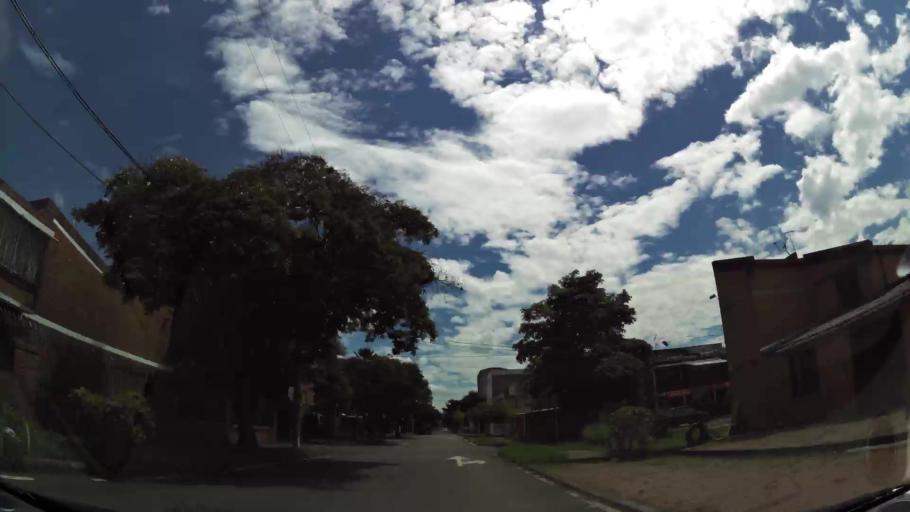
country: CO
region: Valle del Cauca
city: Cali
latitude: 3.3883
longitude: -76.5184
